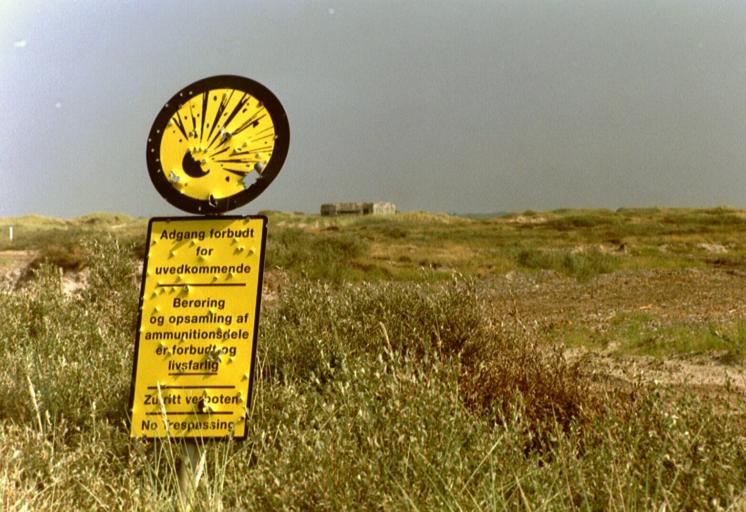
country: DK
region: South Denmark
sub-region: Varde Kommune
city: Oksbol
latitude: 55.5868
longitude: 8.1481
